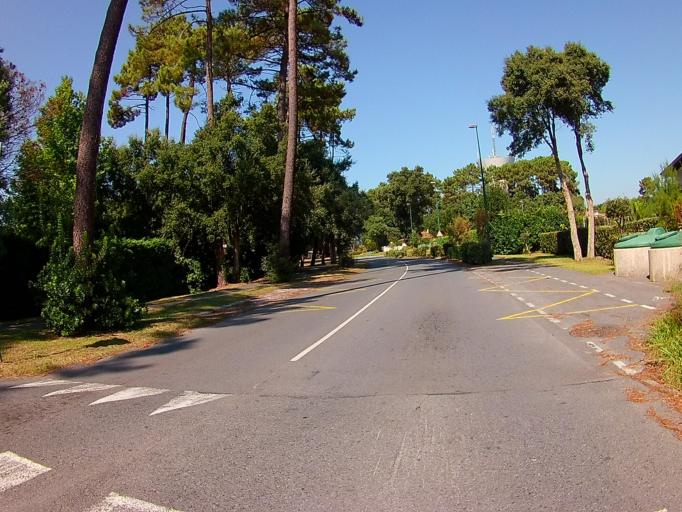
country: FR
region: Aquitaine
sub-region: Departement des Landes
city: Labenne
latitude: 43.5953
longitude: -1.4320
